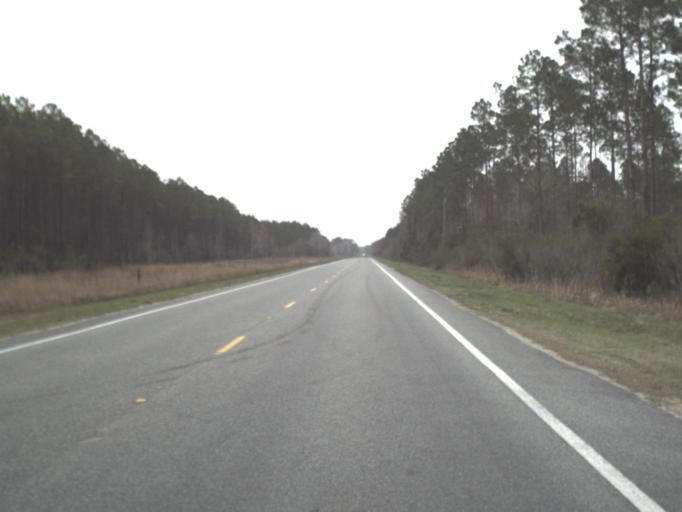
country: US
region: Florida
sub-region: Leon County
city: Woodville
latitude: 30.1955
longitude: -84.1424
